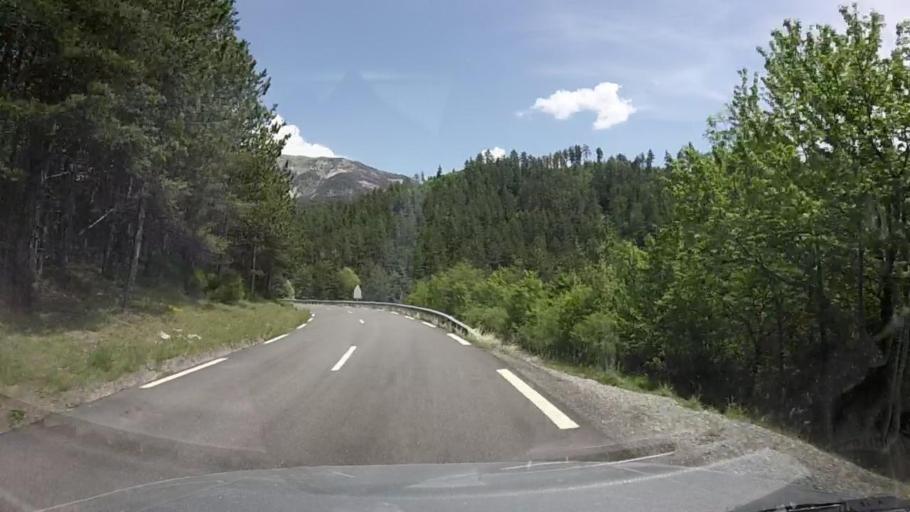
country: FR
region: Provence-Alpes-Cote d'Azur
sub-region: Departement des Alpes-de-Haute-Provence
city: Le Brusquet
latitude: 44.2389
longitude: 6.3600
